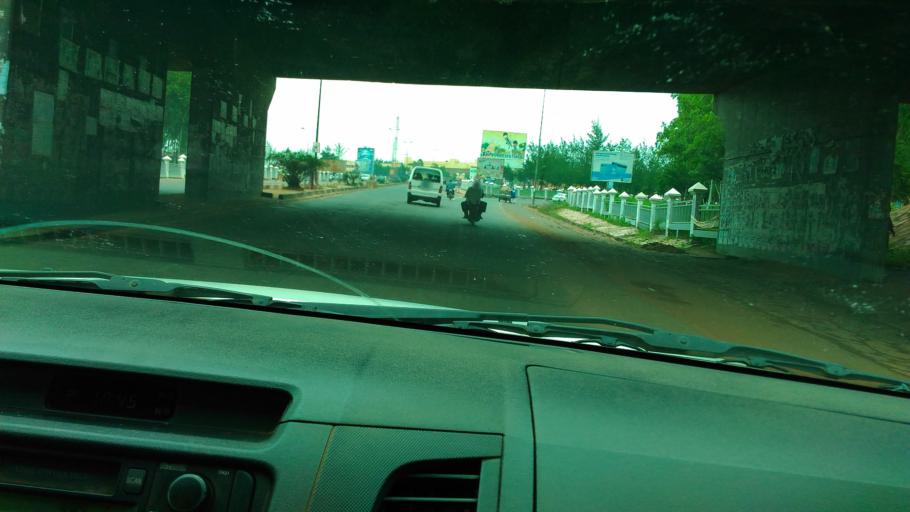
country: ML
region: Bamako
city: Bamako
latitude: 12.6088
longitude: -7.9973
